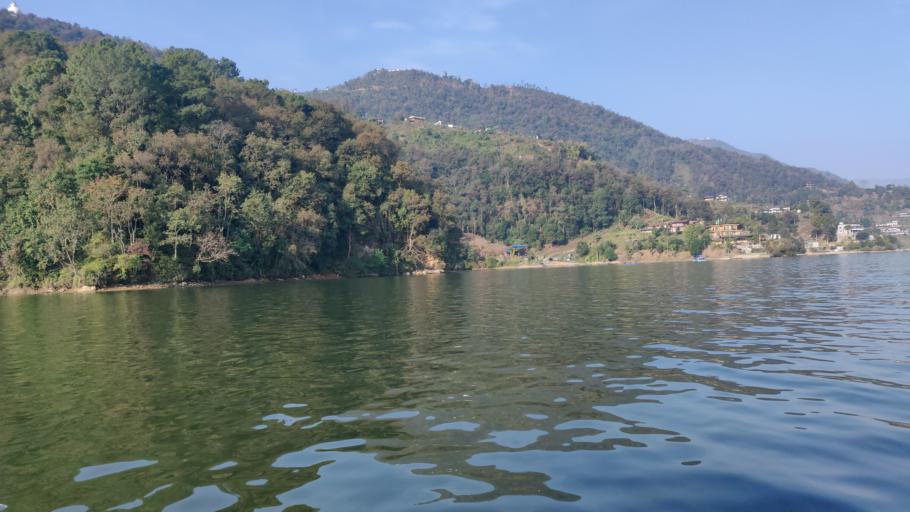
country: NP
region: Western Region
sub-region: Gandaki Zone
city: Pokhara
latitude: 28.2072
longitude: 83.9520
